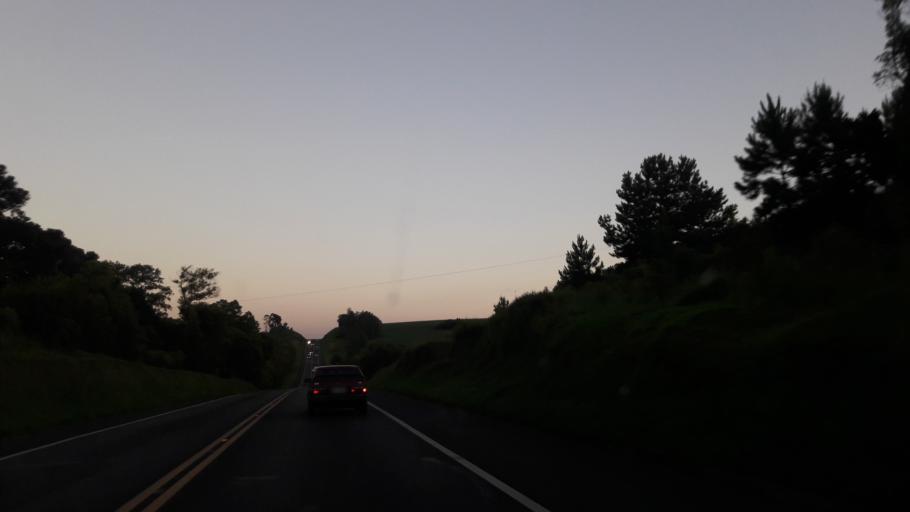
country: BR
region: Parana
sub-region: Palmeira
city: Palmeira
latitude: -25.4250
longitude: -50.0725
